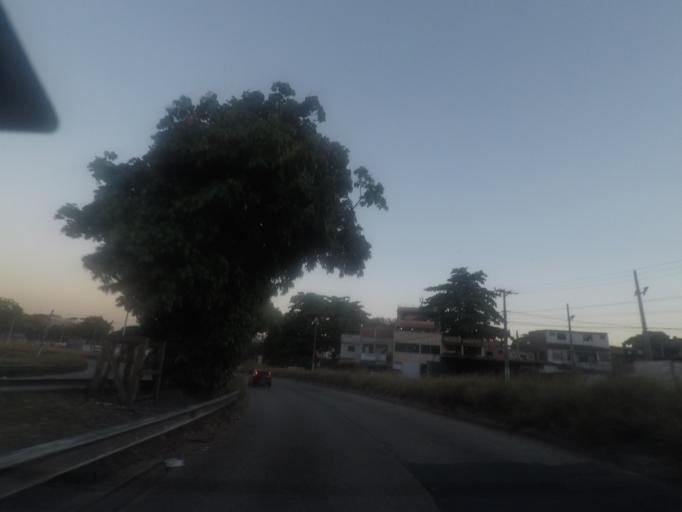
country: BR
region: Rio de Janeiro
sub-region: Duque De Caxias
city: Duque de Caxias
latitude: -22.8176
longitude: -43.2889
